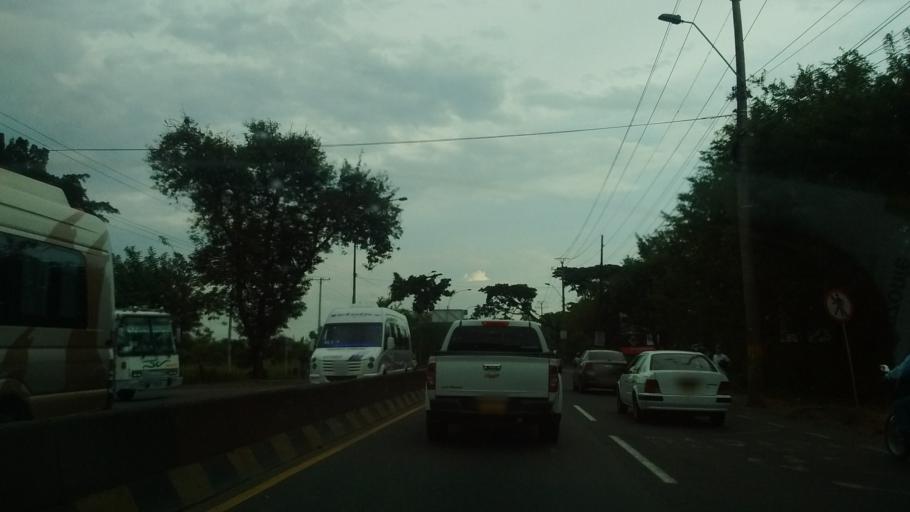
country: CO
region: Valle del Cauca
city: Cali
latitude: 3.3593
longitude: -76.5240
